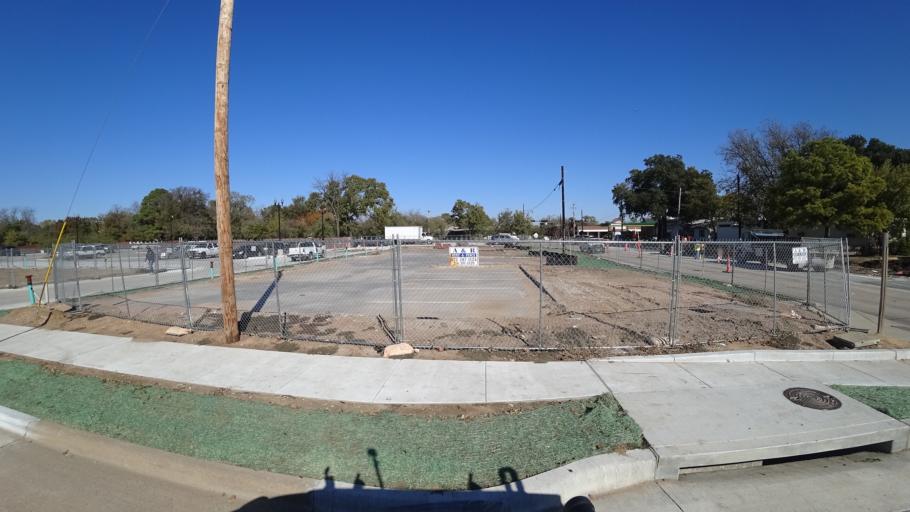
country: US
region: Texas
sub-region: Denton County
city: Lewisville
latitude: 33.0482
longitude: -96.9943
